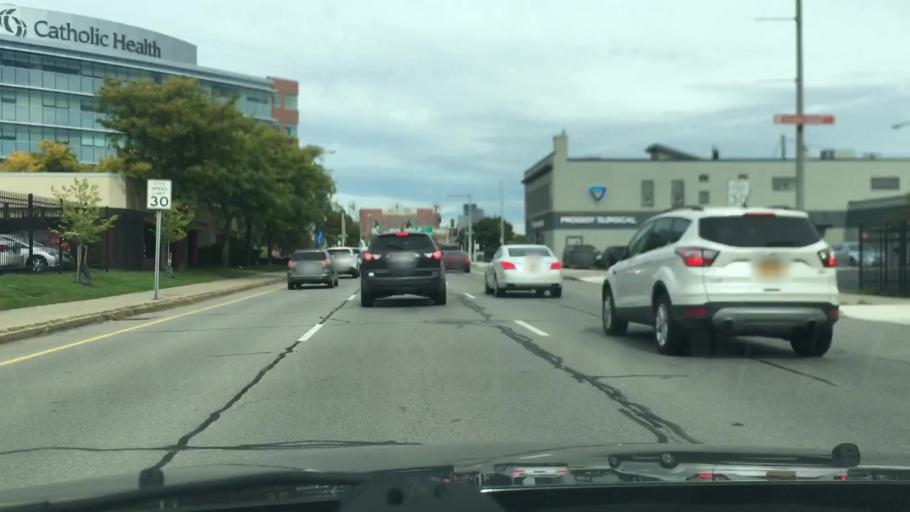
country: US
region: New York
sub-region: Erie County
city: Buffalo
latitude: 42.8895
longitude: -78.8680
